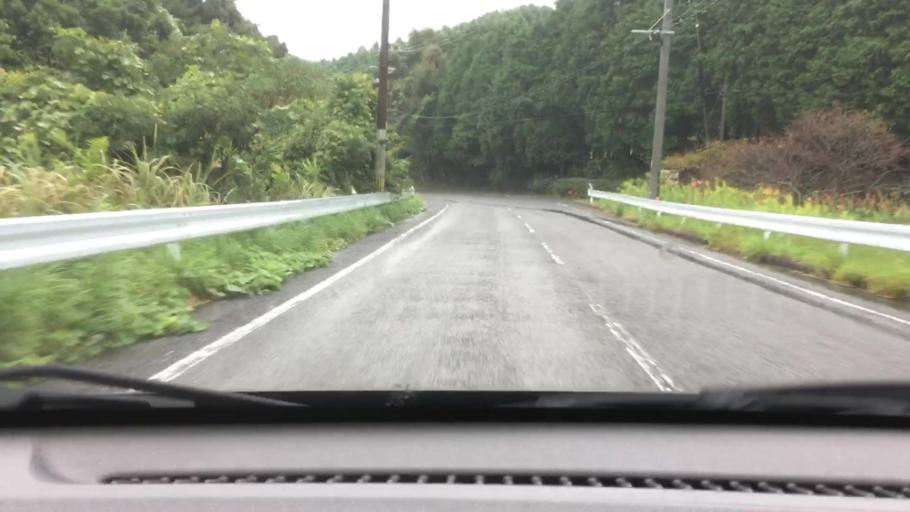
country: JP
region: Nagasaki
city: Togitsu
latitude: 32.8782
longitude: 129.7603
